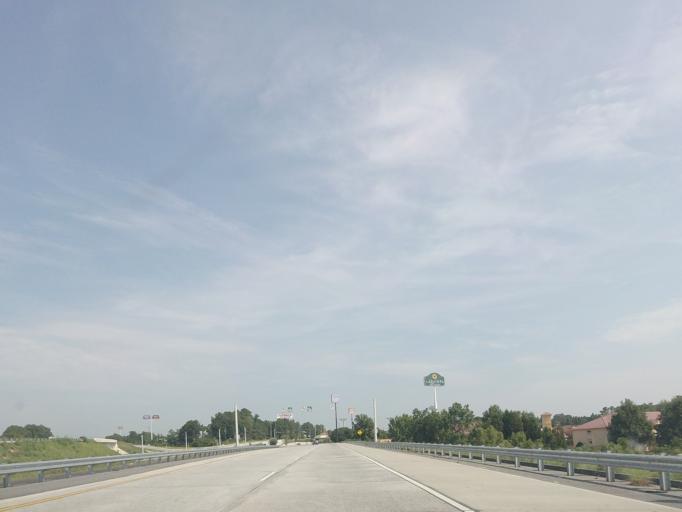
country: US
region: Georgia
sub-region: Bibb County
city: Macon
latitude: 32.9022
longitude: -83.6852
